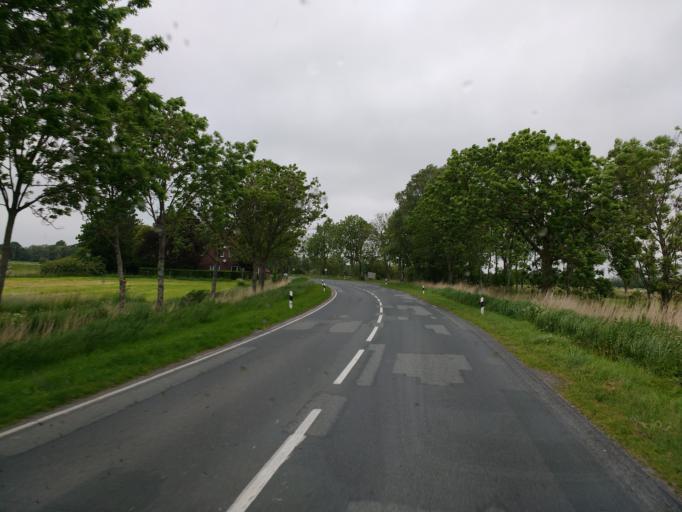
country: DE
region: Lower Saxony
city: Jever
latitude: 53.6263
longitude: 7.9279
